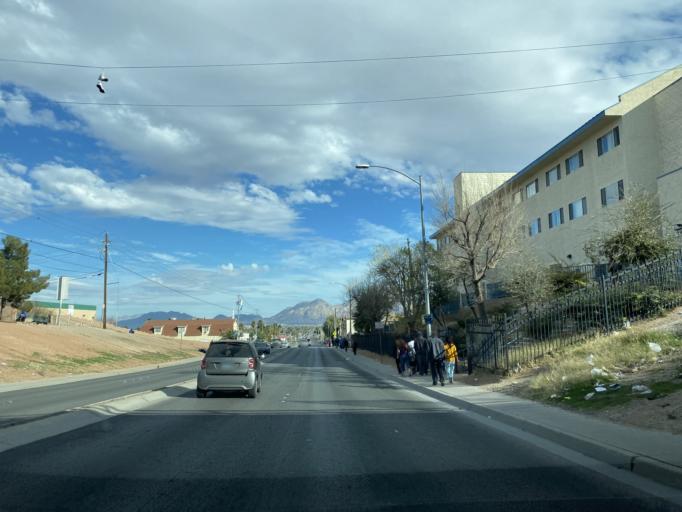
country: US
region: Nevada
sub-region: Clark County
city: Las Vegas
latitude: 36.1883
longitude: -115.1412
